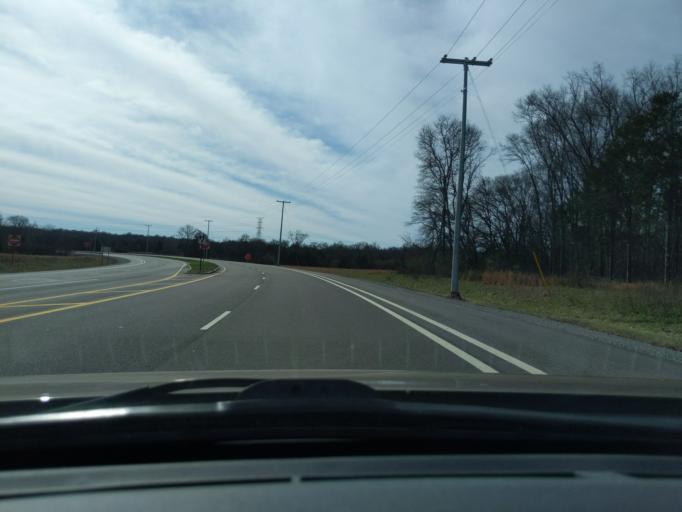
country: US
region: Tennessee
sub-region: Wilson County
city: Mount Juliet
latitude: 36.2041
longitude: -86.4979
